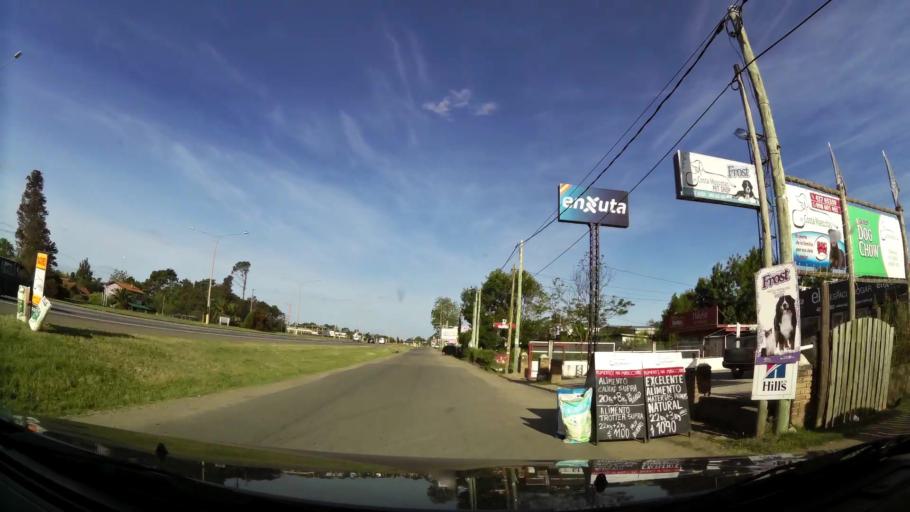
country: UY
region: Canelones
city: Empalme Olmos
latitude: -34.7782
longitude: -55.8581
